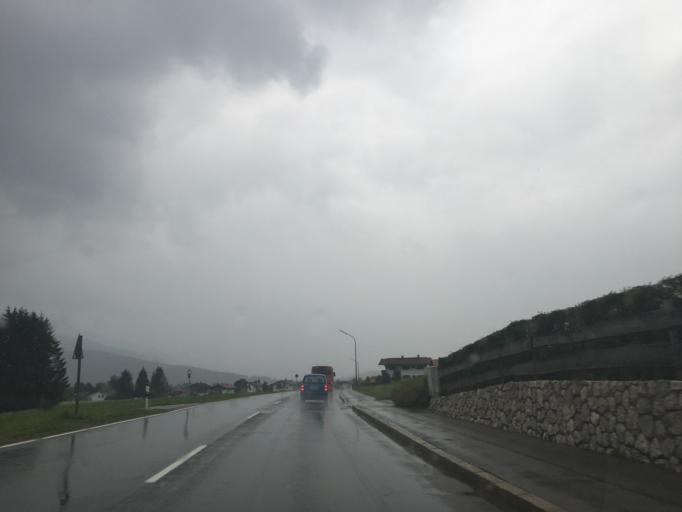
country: DE
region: Bavaria
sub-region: Upper Bavaria
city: Reit im Winkl
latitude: 47.6766
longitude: 12.4932
